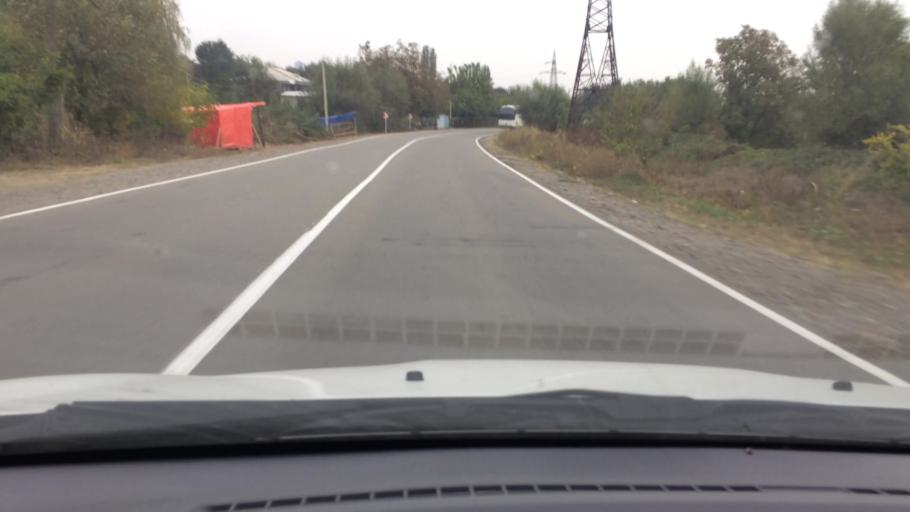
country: GE
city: Naghvarevi
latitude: 41.3218
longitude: 44.7974
